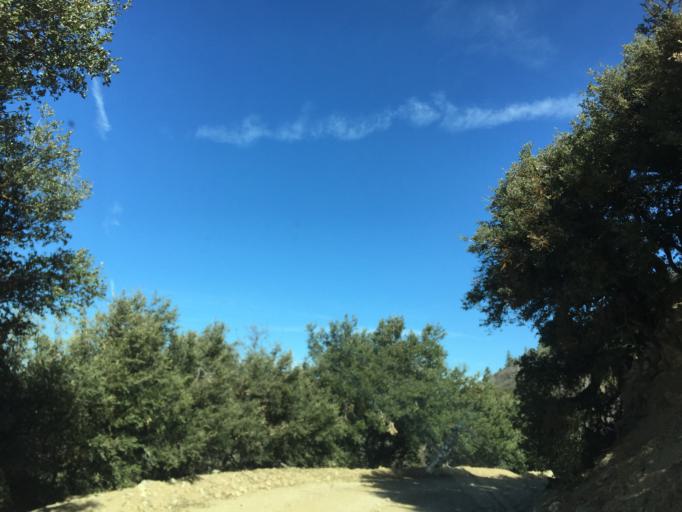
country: US
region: California
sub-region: Kern County
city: Stallion Springs
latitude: 34.9254
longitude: -118.6490
